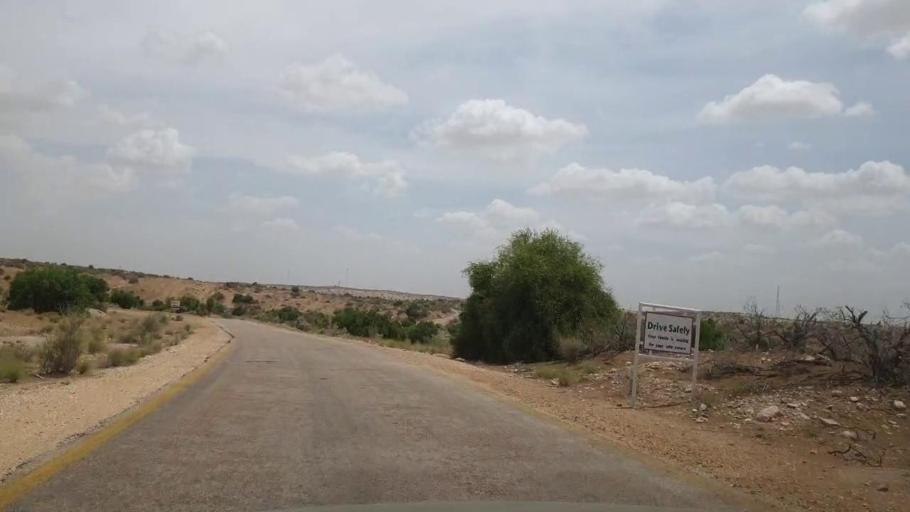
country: PK
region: Sindh
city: Kot Diji
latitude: 27.1488
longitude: 69.2251
